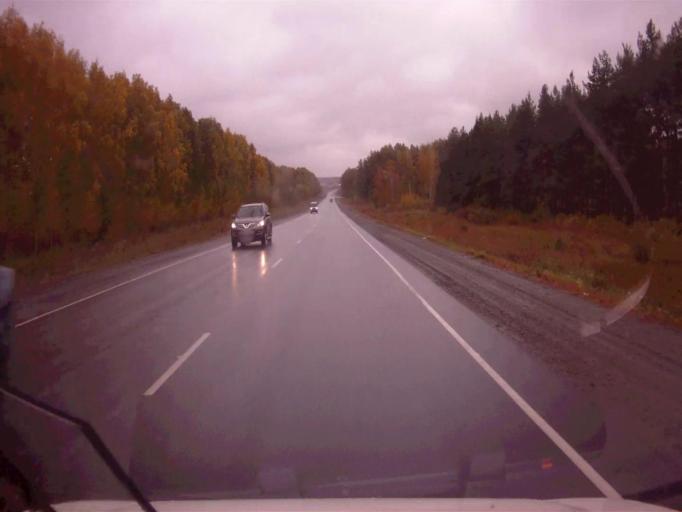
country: RU
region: Chelyabinsk
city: Roshchino
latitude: 55.3630
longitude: 61.2101
